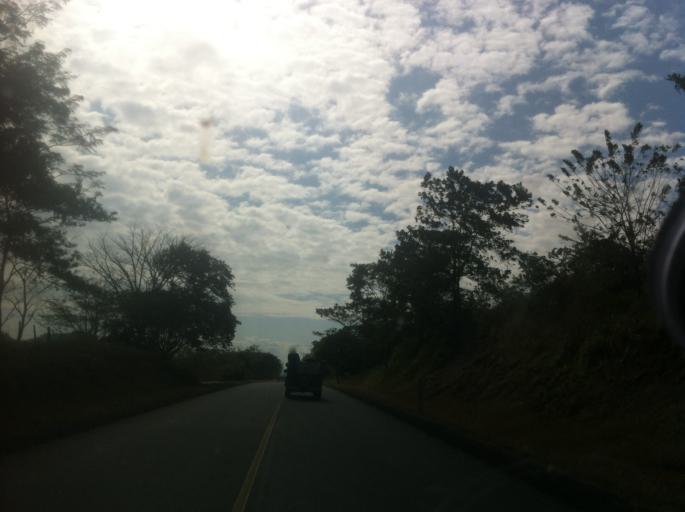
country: NI
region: Rio San Juan
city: San Miguelito
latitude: 11.3806
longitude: -84.7870
